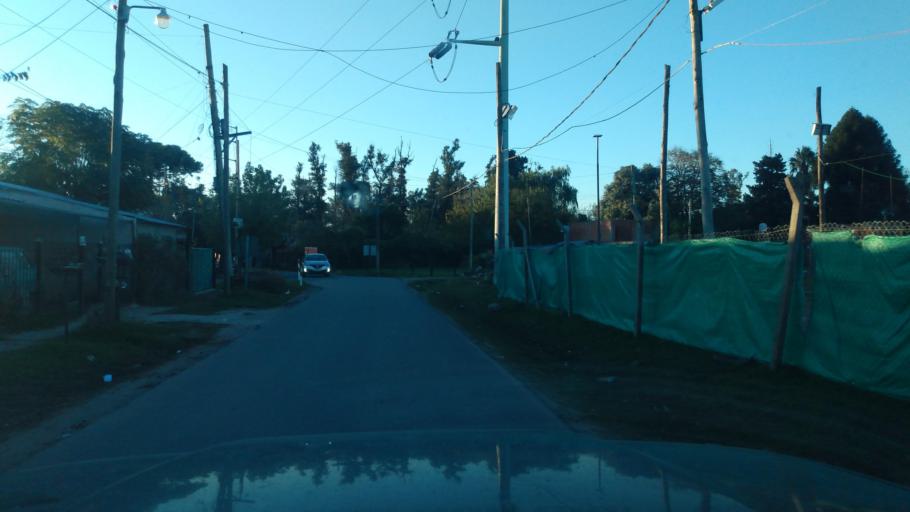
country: AR
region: Buenos Aires
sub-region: Partido de Merlo
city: Merlo
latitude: -34.6565
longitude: -58.7465
